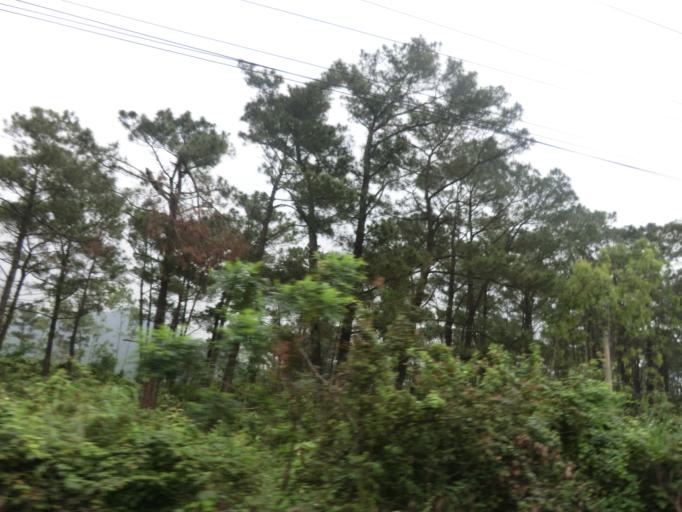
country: VN
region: Quang Binh
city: Ba Don
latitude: 17.6650
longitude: 106.4297
